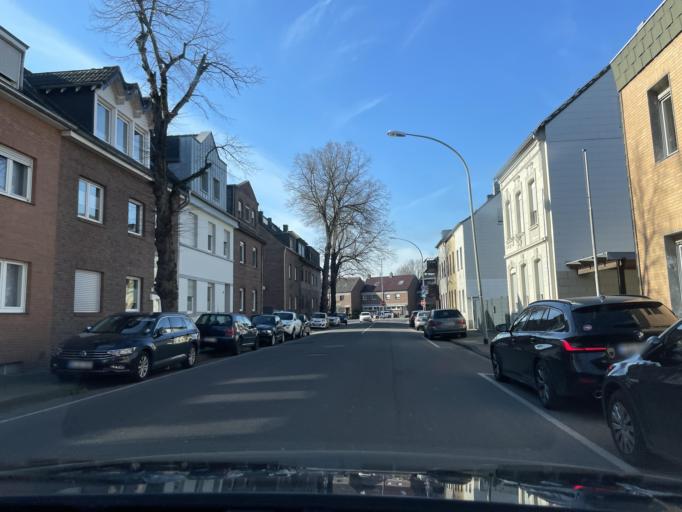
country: DE
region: North Rhine-Westphalia
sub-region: Regierungsbezirk Dusseldorf
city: Monchengladbach
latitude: 51.2173
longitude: 6.4495
